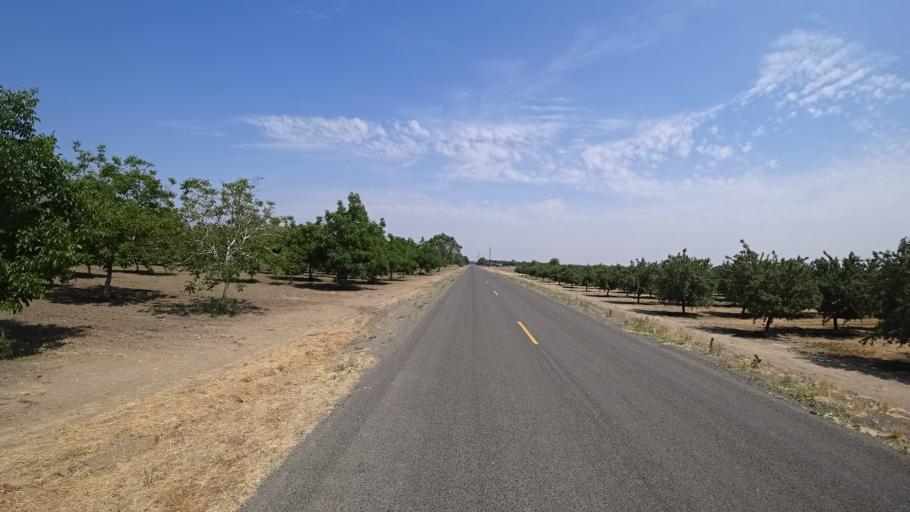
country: US
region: California
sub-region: Fresno County
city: Laton
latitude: 36.3918
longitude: -119.7450
